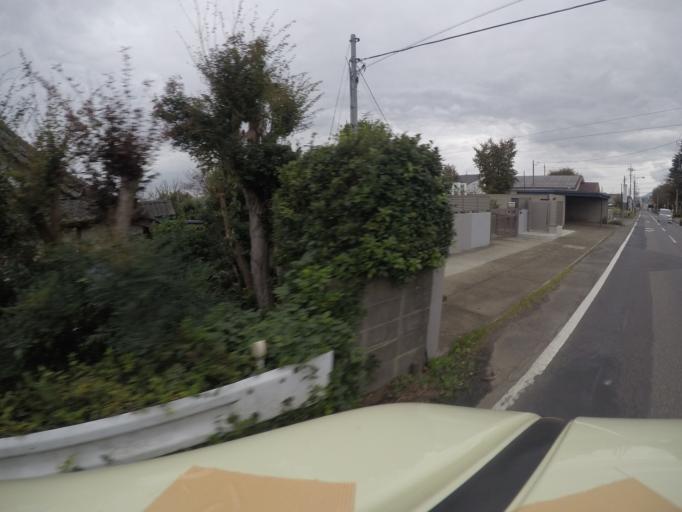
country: JP
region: Ibaraki
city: Naka
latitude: 36.0835
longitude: 140.1303
